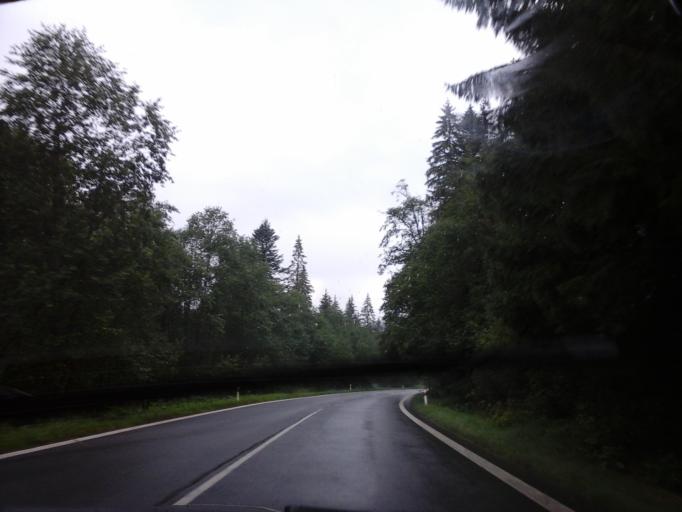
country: PL
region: Lesser Poland Voivodeship
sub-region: Powiat tatrzanski
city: Bukowina Tatrzanska
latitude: 49.2718
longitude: 20.1534
